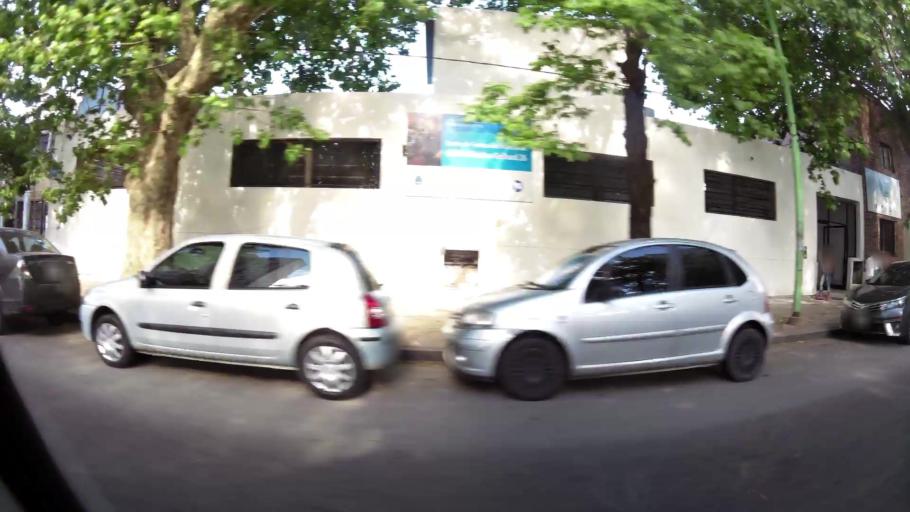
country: AR
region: Buenos Aires
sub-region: Partido de La Plata
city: La Plata
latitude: -34.9005
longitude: -57.9493
